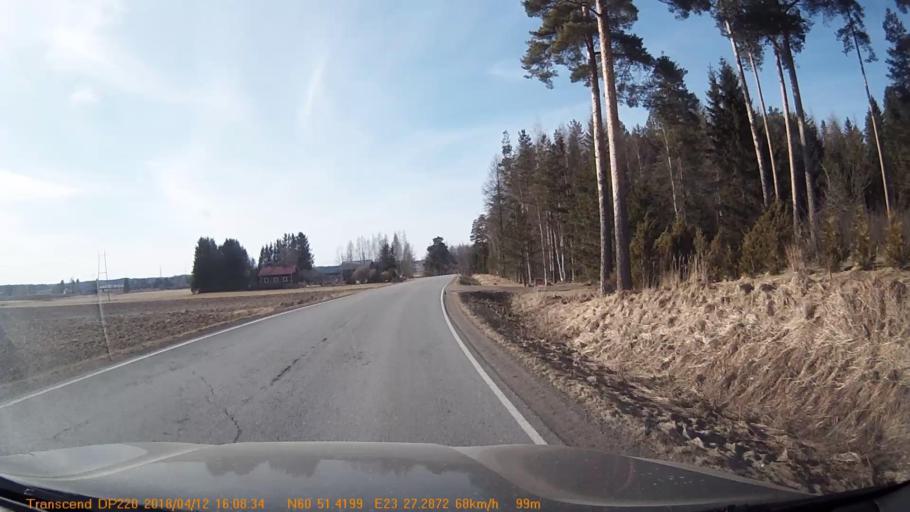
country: FI
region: Haeme
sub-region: Forssa
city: Jokioinen
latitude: 60.8569
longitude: 23.4549
